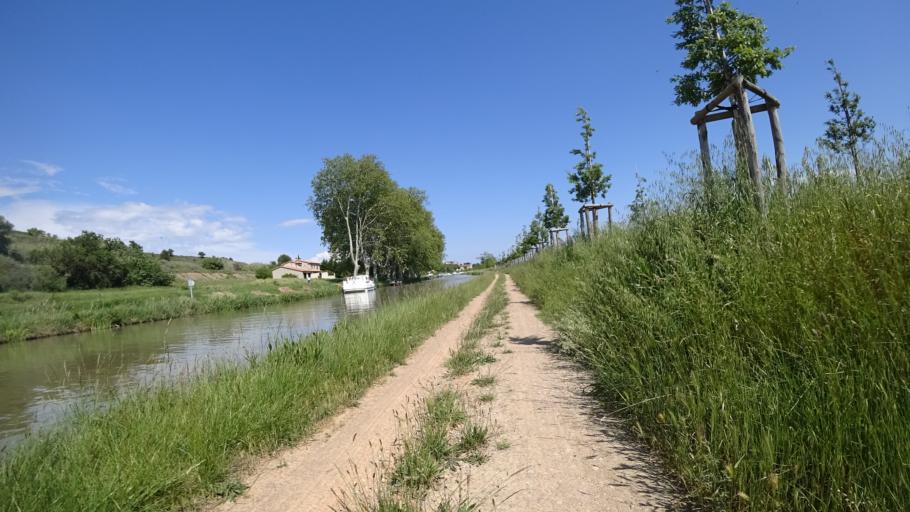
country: FR
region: Languedoc-Roussillon
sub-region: Departement de l'Aude
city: Canet
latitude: 43.2481
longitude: 2.8487
